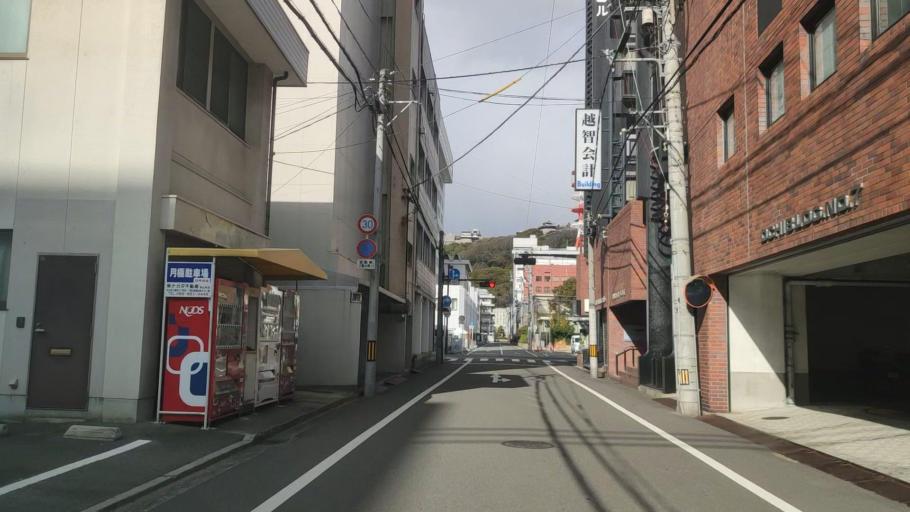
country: JP
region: Ehime
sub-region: Shikoku-chuo Shi
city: Matsuyama
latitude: 33.8379
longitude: 132.7658
